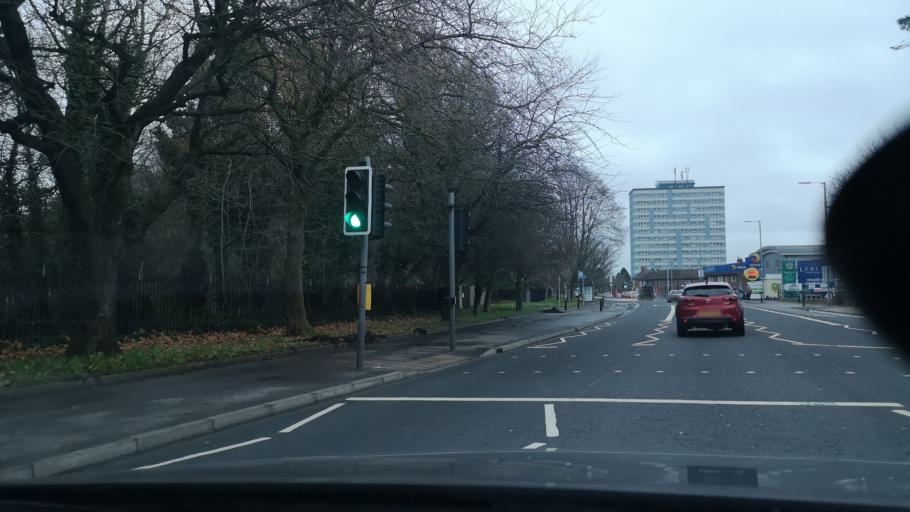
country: GB
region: Northern Ireland
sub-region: Castlereagh District
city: Dundonald
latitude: 54.5944
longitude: -5.8272
